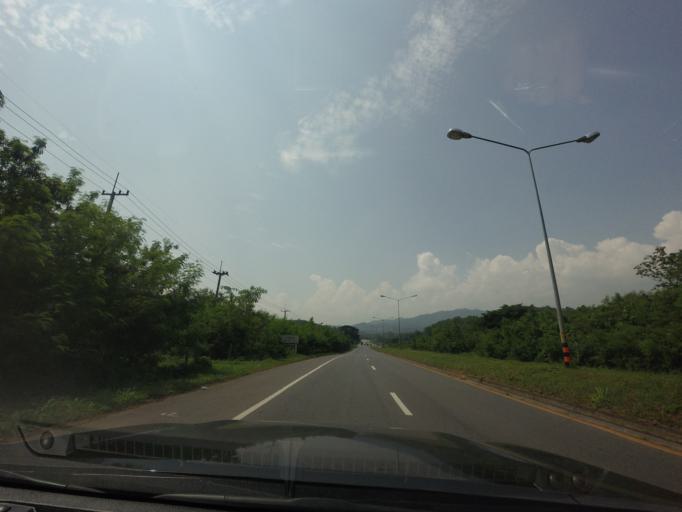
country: TH
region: Phrae
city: Den Chai
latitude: 17.9449
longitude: 100.0655
